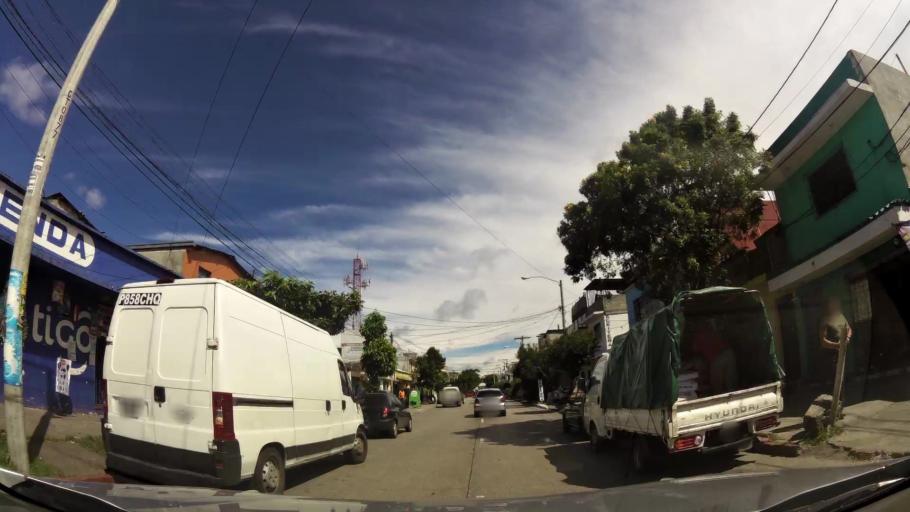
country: GT
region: Guatemala
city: Guatemala City
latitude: 14.5973
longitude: -90.5464
